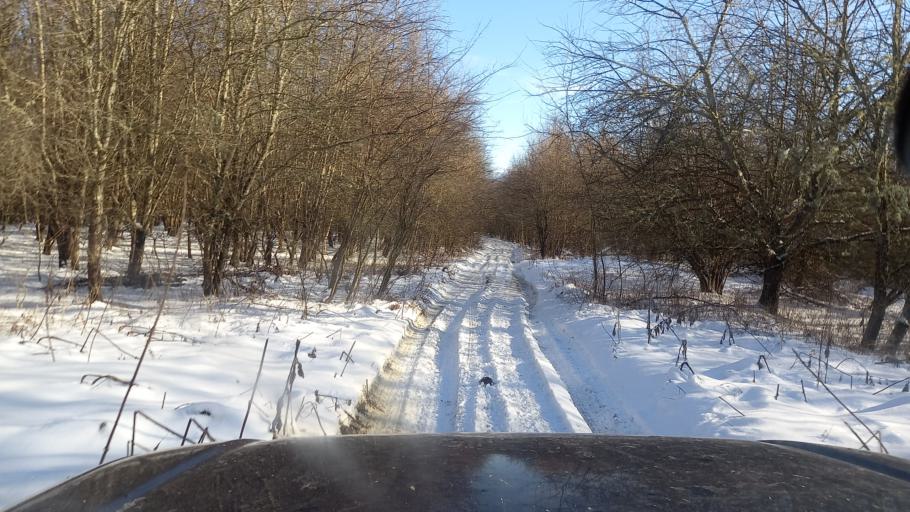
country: RU
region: Adygeya
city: Kamennomostskiy
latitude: 44.2115
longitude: 40.1416
